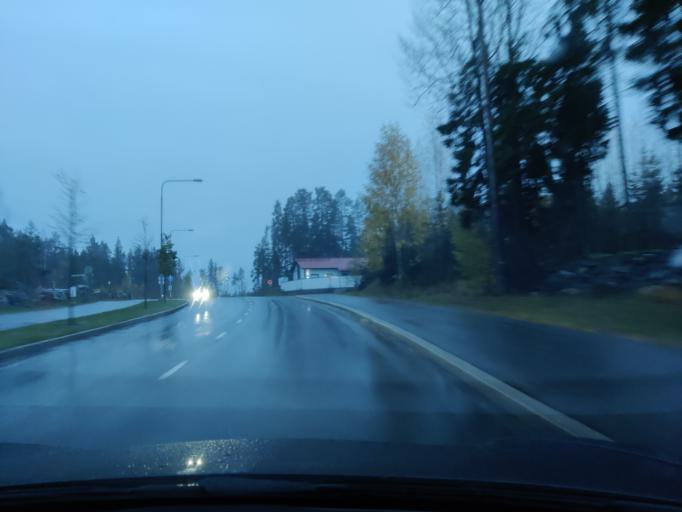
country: FI
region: Northern Savo
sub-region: Kuopio
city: Kuopio
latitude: 62.8293
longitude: 27.7024
